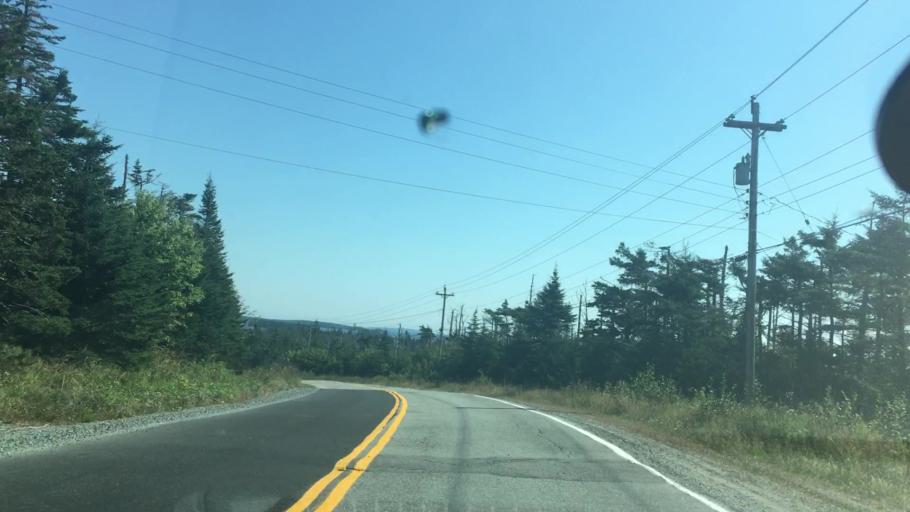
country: CA
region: Nova Scotia
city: New Glasgow
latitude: 44.9156
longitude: -62.3171
